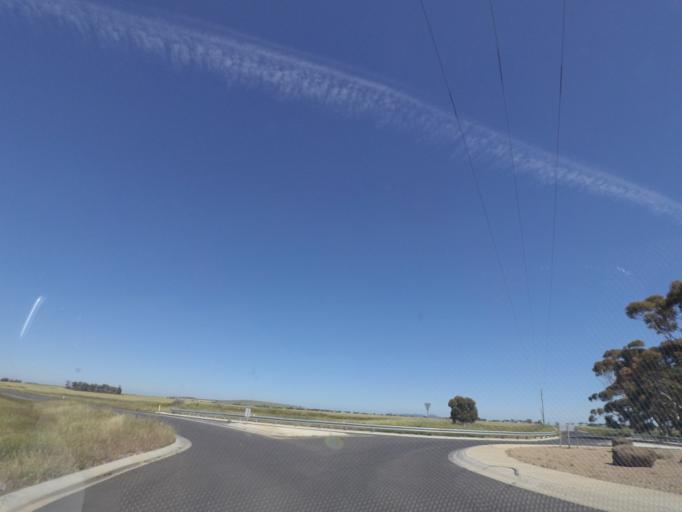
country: AU
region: Victoria
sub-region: Moorabool
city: Bacchus Marsh
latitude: -37.7384
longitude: 144.3919
